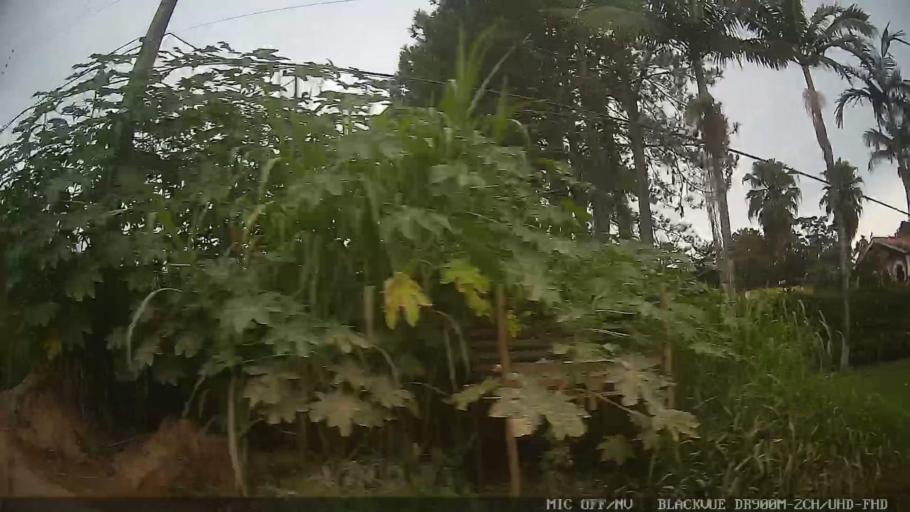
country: BR
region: Sao Paulo
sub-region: Atibaia
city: Atibaia
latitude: -23.1843
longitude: -46.6133
